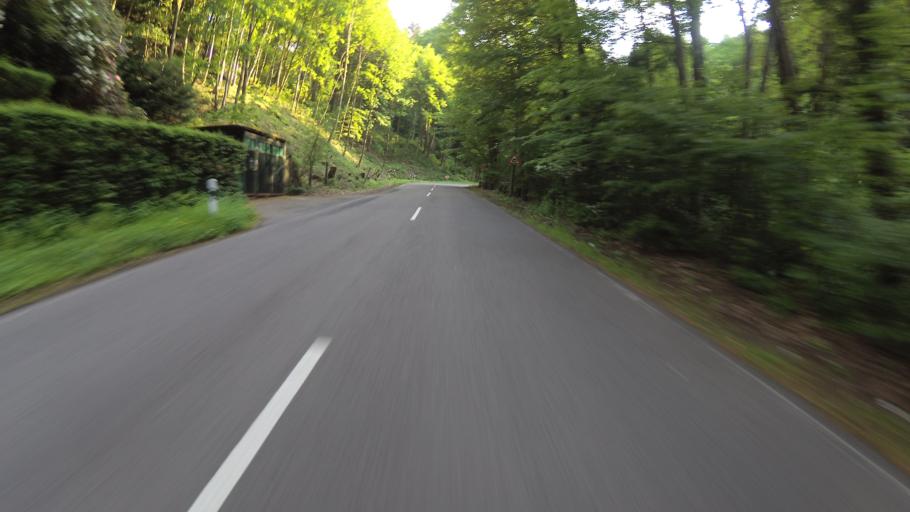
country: DE
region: Rheinland-Pfalz
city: Pirmasens
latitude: 49.2043
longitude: 7.6166
